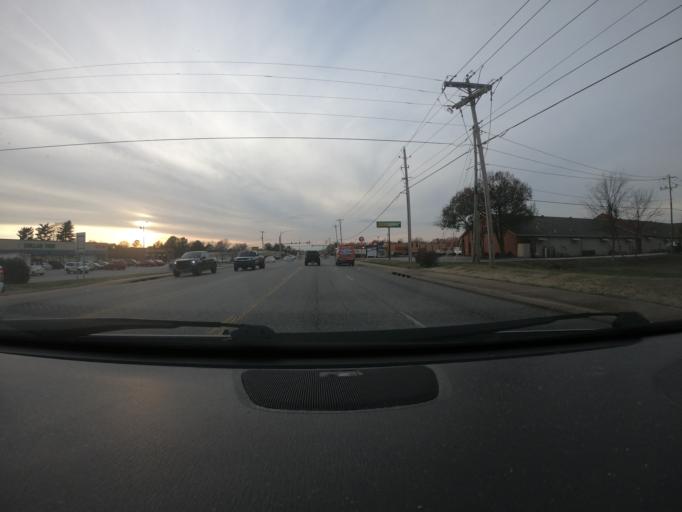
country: US
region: Arkansas
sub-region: Benton County
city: Rogers
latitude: 36.3342
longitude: -94.1501
